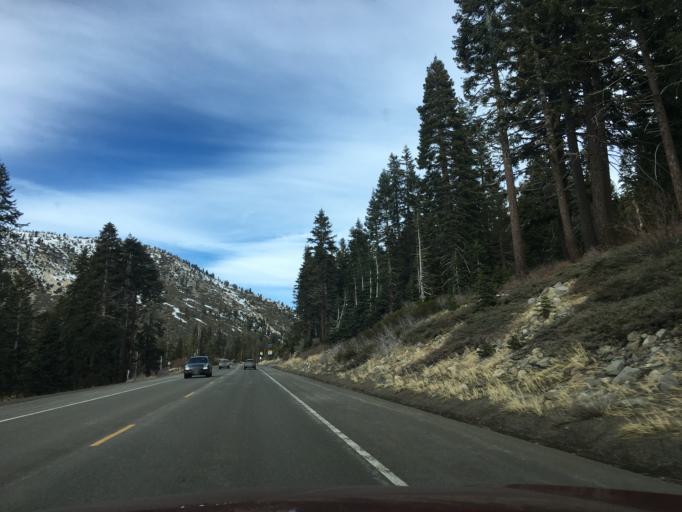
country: US
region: Nevada
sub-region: Washoe County
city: Incline Village
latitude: 39.2790
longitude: -119.9340
